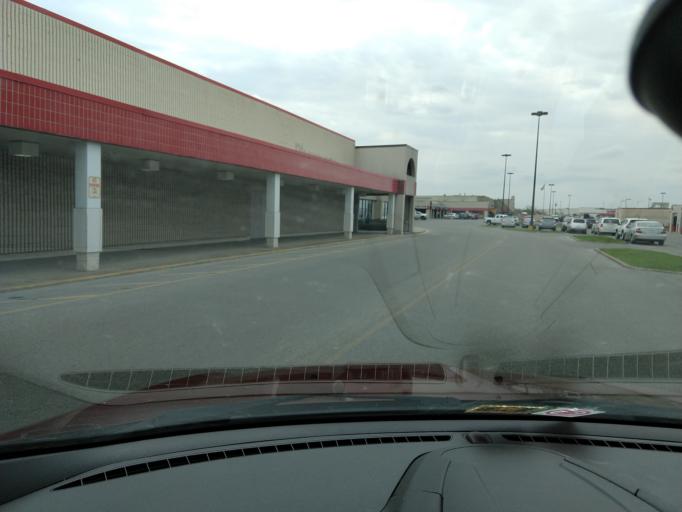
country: US
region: West Virginia
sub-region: Harrison County
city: Bridgeport
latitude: 39.2789
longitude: -80.2802
